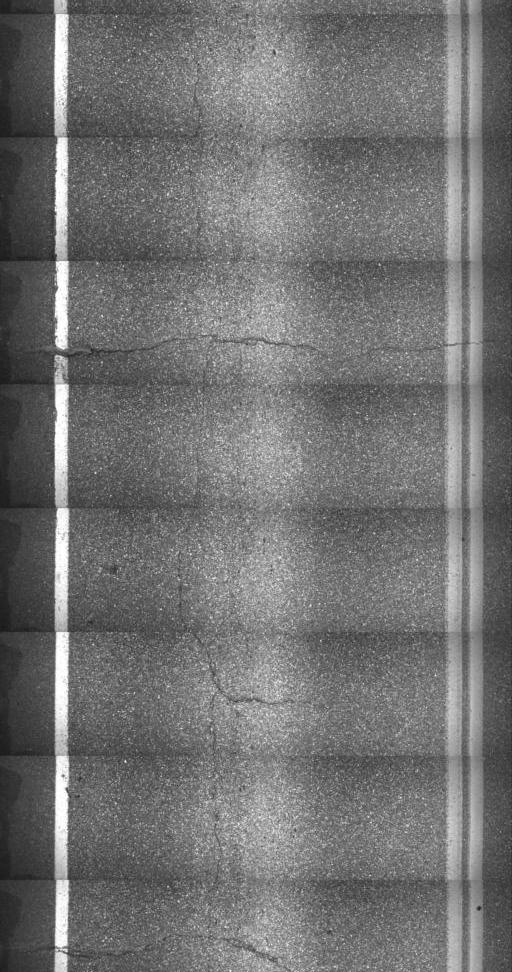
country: US
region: Vermont
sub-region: Lamoille County
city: Morristown
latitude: 44.4753
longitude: -72.6689
